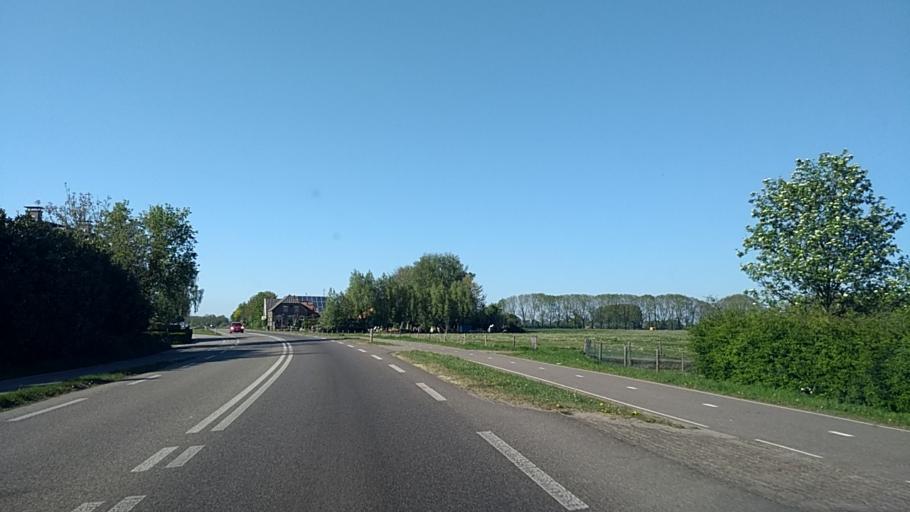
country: NL
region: Gelderland
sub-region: Gemeente Bronckhorst
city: Baak
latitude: 52.0800
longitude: 6.2252
